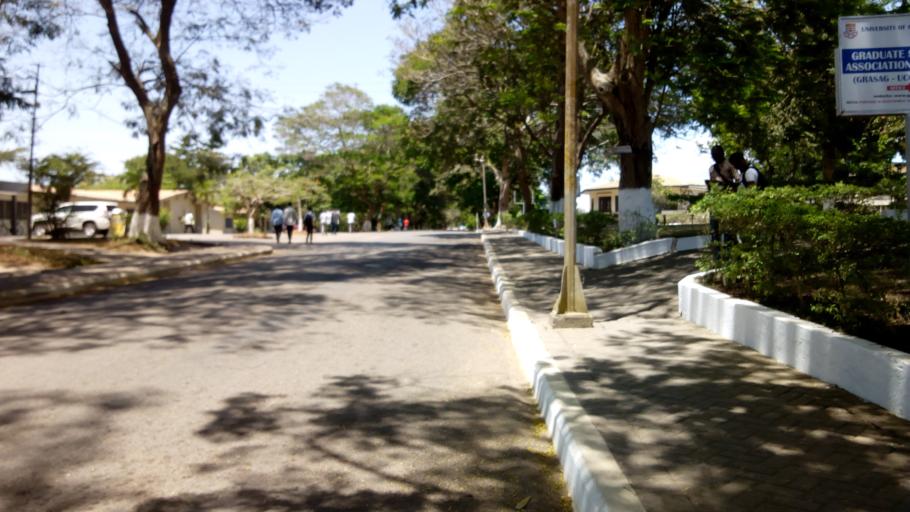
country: GH
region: Central
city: Cape Coast
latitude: 5.1181
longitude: -1.2889
